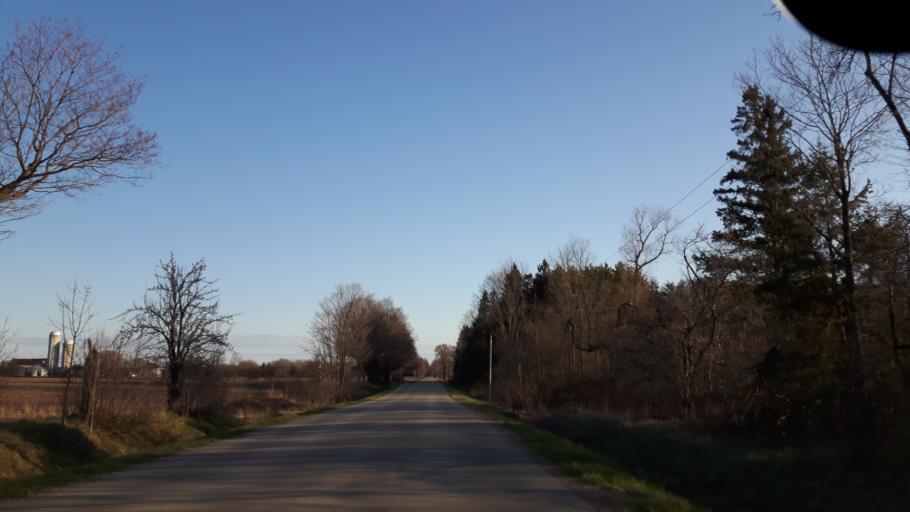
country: CA
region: Ontario
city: Goderich
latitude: 43.6348
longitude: -81.6846
